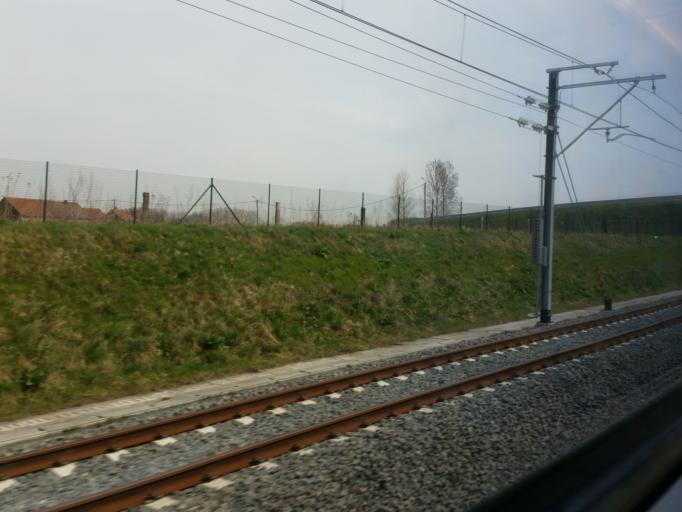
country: BE
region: Flanders
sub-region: Provincie Vlaams-Brabant
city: Ternat
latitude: 50.8539
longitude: 4.1747
